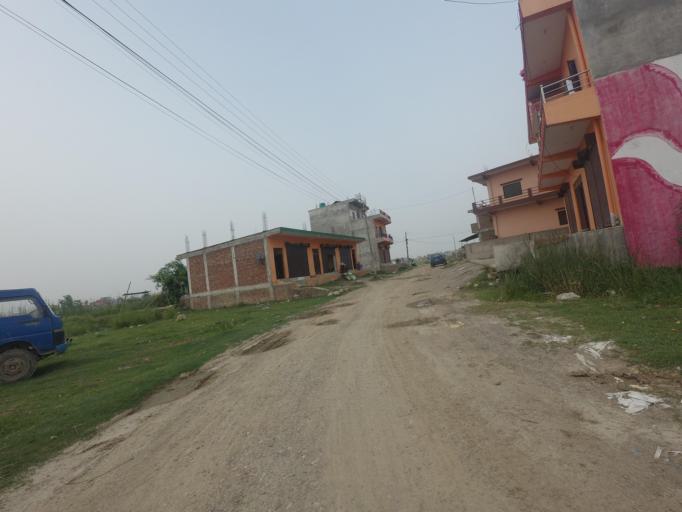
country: NP
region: Western Region
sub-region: Lumbini Zone
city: Bhairahawa
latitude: 27.5116
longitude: 83.4314
